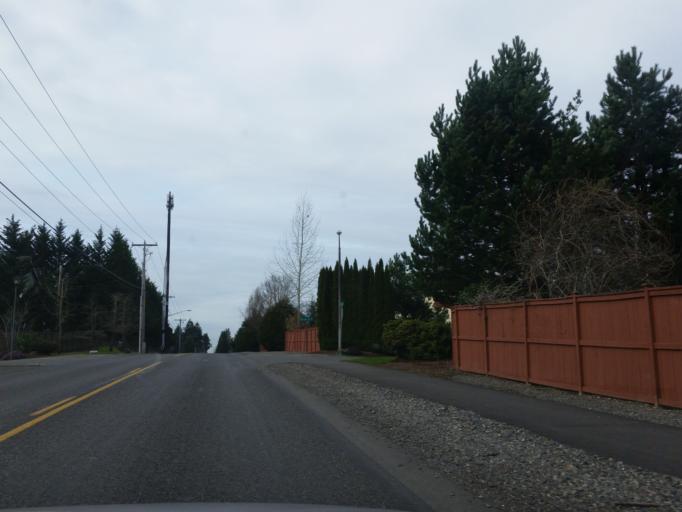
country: US
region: Washington
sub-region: Pierce County
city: South Hill
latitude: 47.1328
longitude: -122.2734
